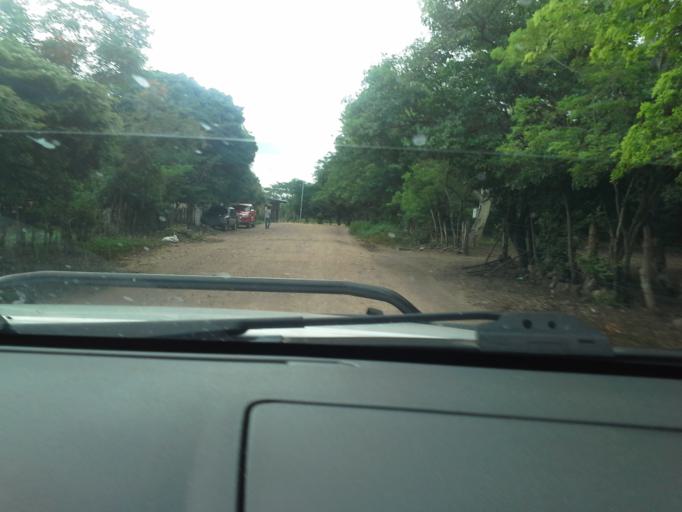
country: NI
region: Matagalpa
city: Ciudad Dario
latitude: 12.8340
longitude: -86.2109
